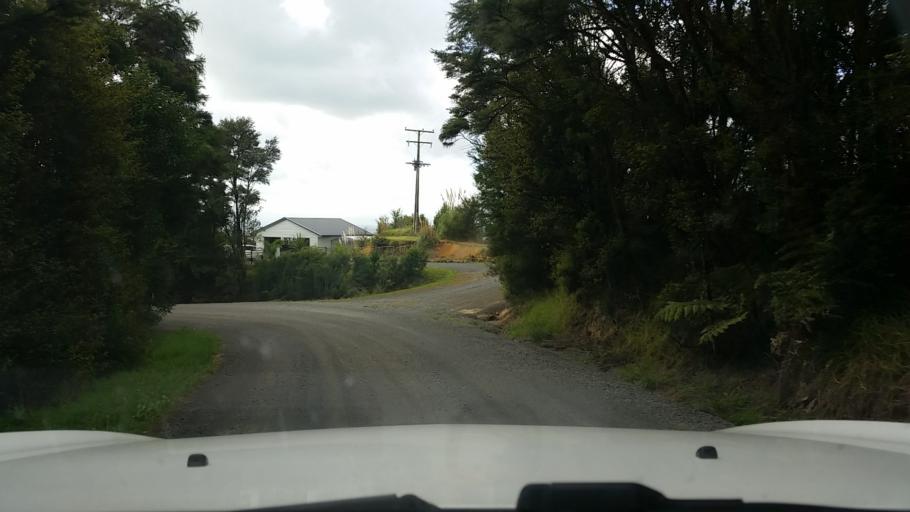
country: NZ
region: Waikato
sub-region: Hauraki District
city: Ngatea
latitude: -37.4499
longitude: 175.4744
